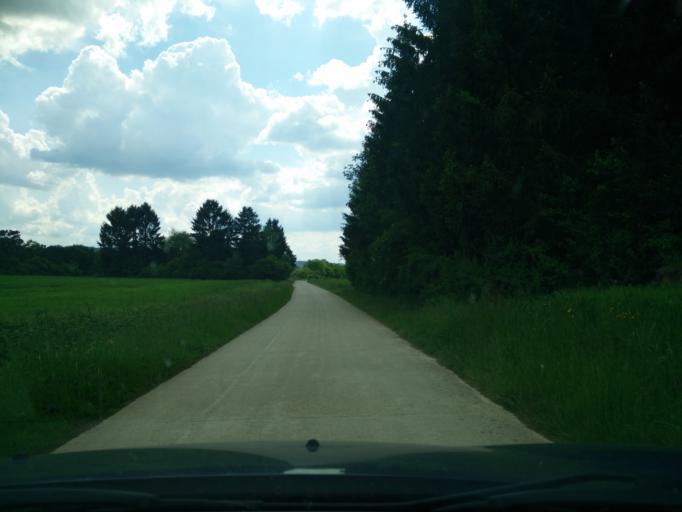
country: FR
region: Champagne-Ardenne
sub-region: Departement des Ardennes
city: Vireux-Molhain
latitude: 50.0796
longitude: 4.6125
